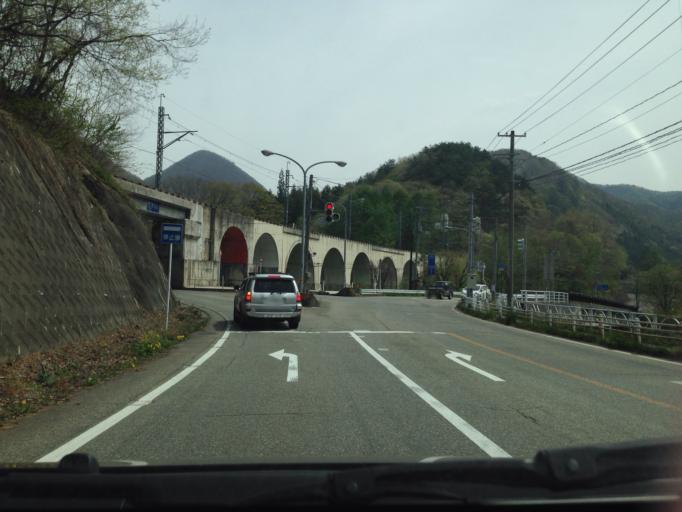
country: JP
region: Tochigi
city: Kuroiso
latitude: 37.1125
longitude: 139.7187
